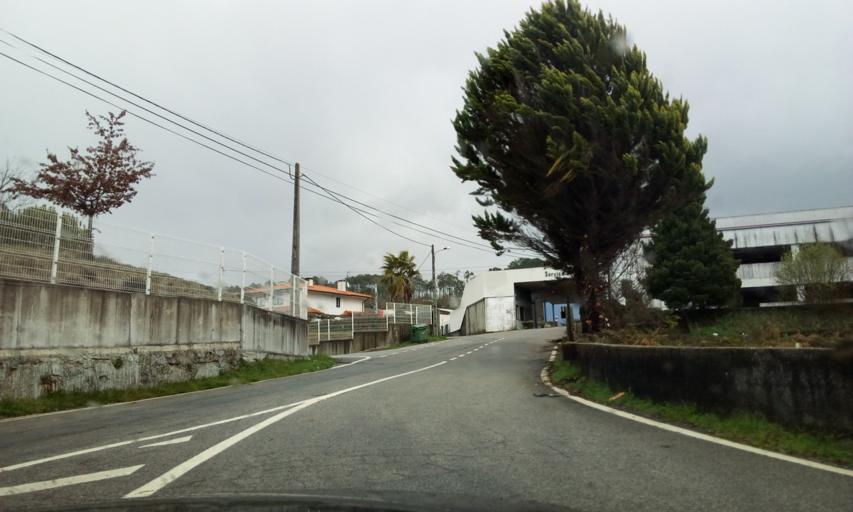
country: PT
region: Viseu
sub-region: Viseu
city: Viseu
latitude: 40.6212
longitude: -7.9188
